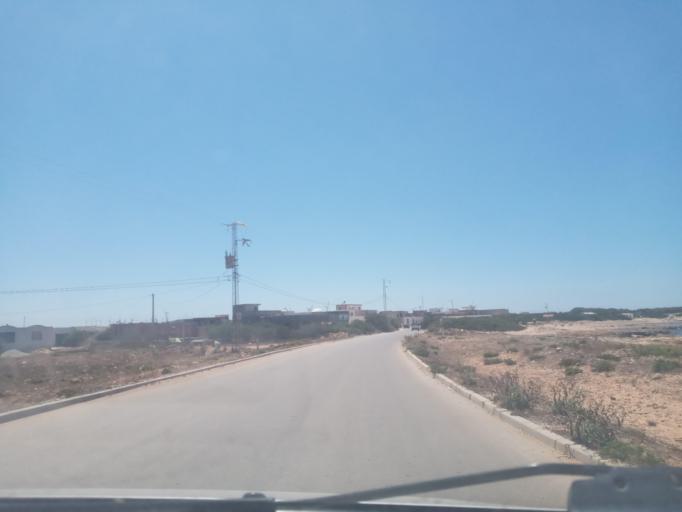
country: TN
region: Nabul
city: El Haouaria
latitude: 37.0494
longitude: 10.9733
